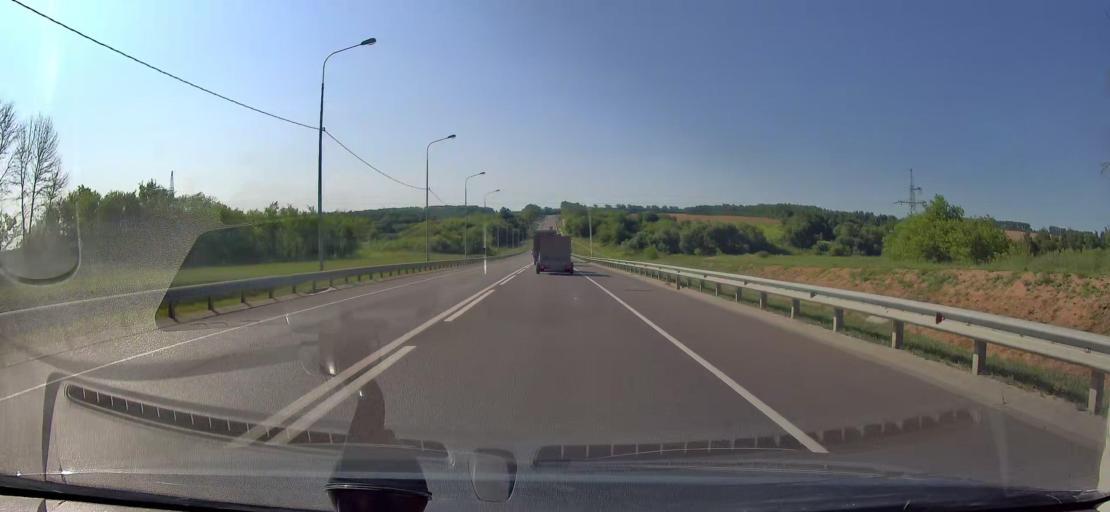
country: RU
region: Orjol
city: Kromy
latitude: 52.6238
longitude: 35.7575
